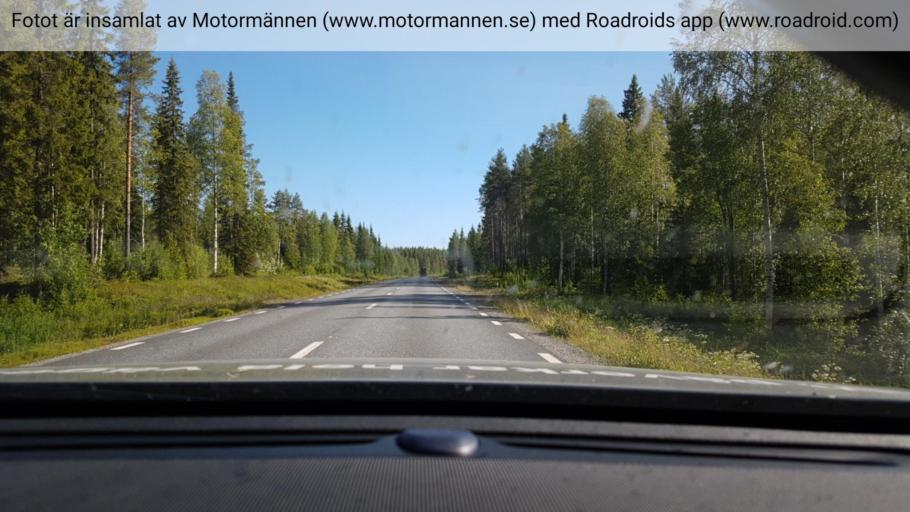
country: SE
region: Vaesterbotten
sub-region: Bjurholms Kommun
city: Bjurholm
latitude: 64.3705
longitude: 19.1412
